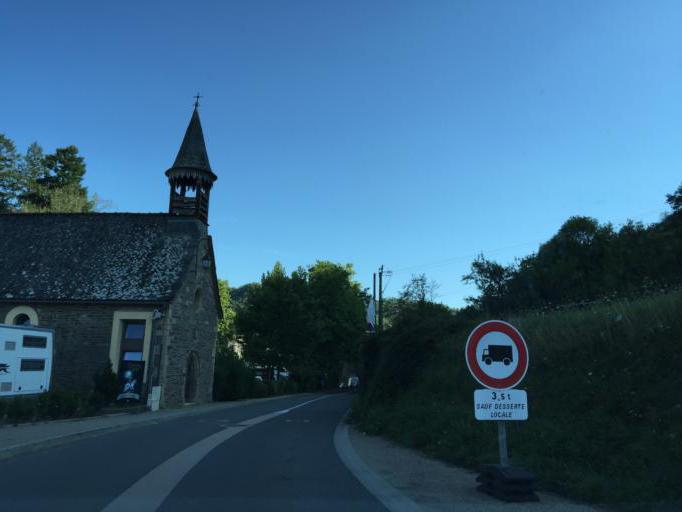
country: FR
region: Midi-Pyrenees
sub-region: Departement de l'Aveyron
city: Espalion
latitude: 44.5576
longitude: 2.6705
